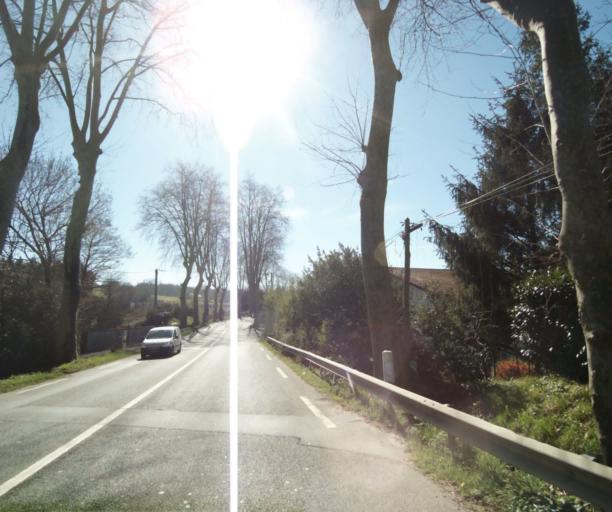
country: FR
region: Aquitaine
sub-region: Departement des Pyrenees-Atlantiques
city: Ciboure
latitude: 43.3703
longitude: -1.6826
